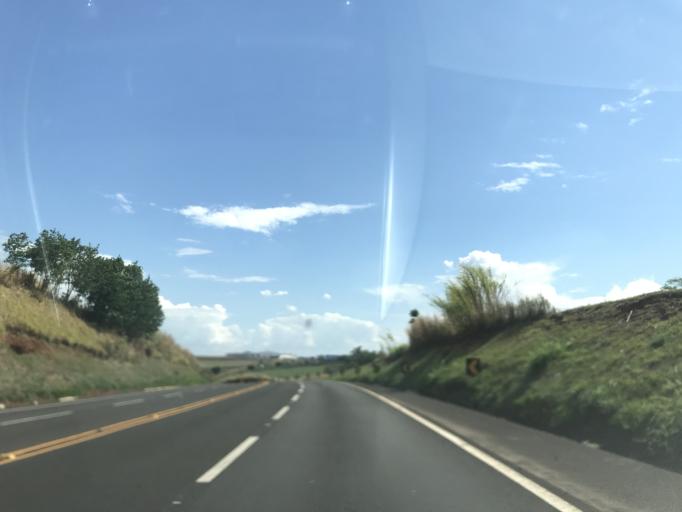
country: BR
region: Parana
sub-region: Mandaguari
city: Mandaguari
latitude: -23.4963
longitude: -51.6478
